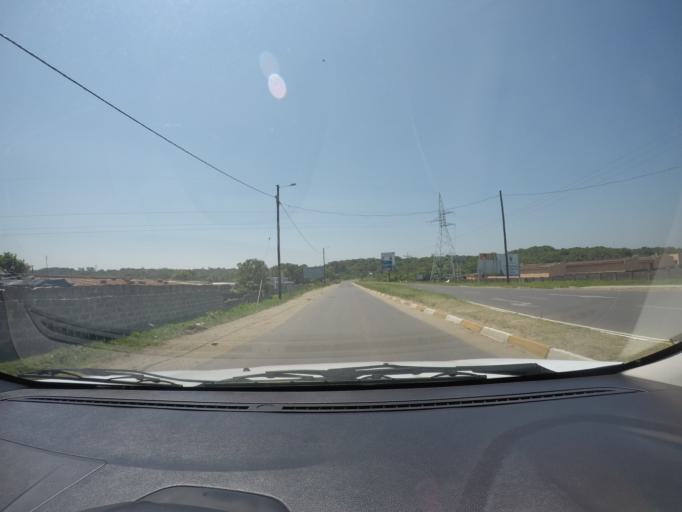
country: ZA
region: KwaZulu-Natal
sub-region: uThungulu District Municipality
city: eSikhawini
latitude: -28.8569
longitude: 31.9233
